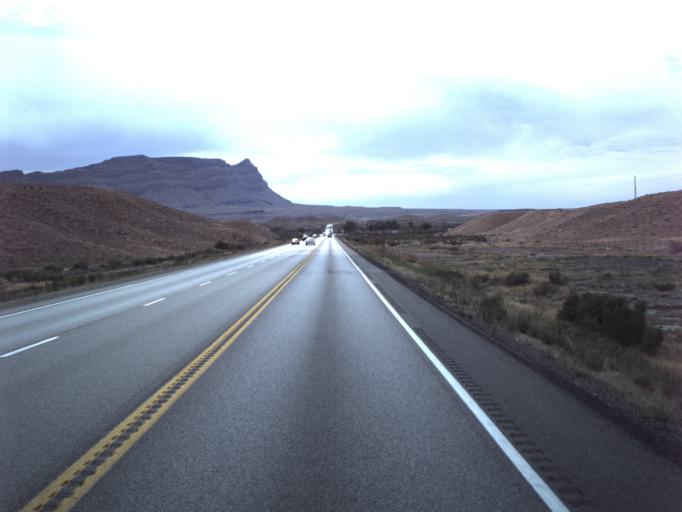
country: US
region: Utah
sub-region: Carbon County
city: East Carbon City
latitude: 39.2736
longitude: -110.3467
